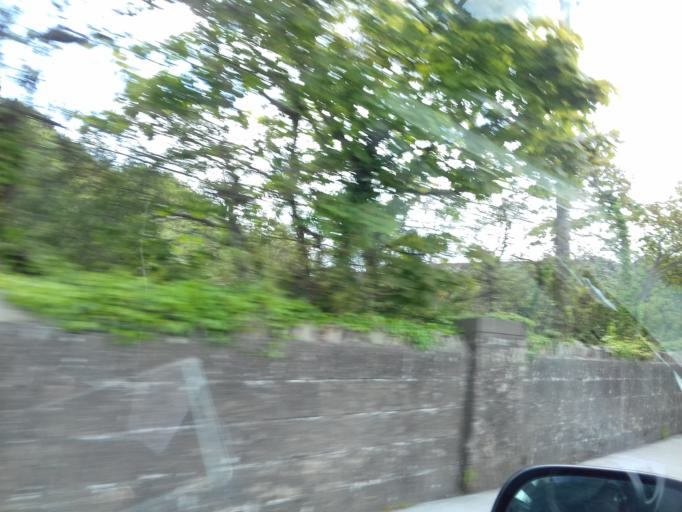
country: IE
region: Leinster
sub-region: Loch Garman
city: Loch Garman
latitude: 52.3451
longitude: -6.4555
